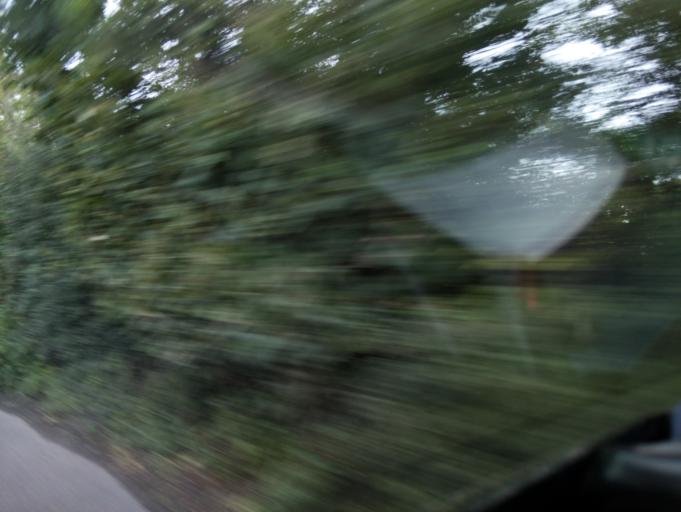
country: GB
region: England
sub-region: Devon
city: Exminster
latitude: 50.6735
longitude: -3.4862
